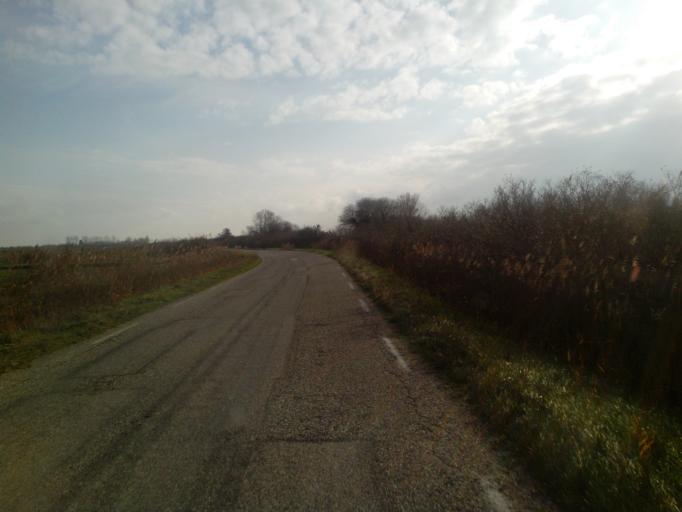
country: FR
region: Languedoc-Roussillon
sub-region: Departement du Gard
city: Saint-Gilles
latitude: 43.5950
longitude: 4.4910
